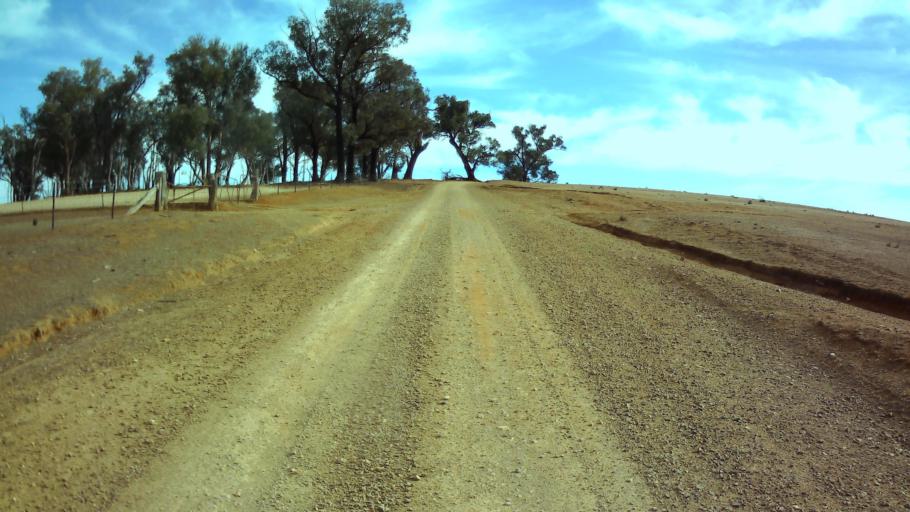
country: AU
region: New South Wales
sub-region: Weddin
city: Grenfell
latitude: -33.8951
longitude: 148.2041
